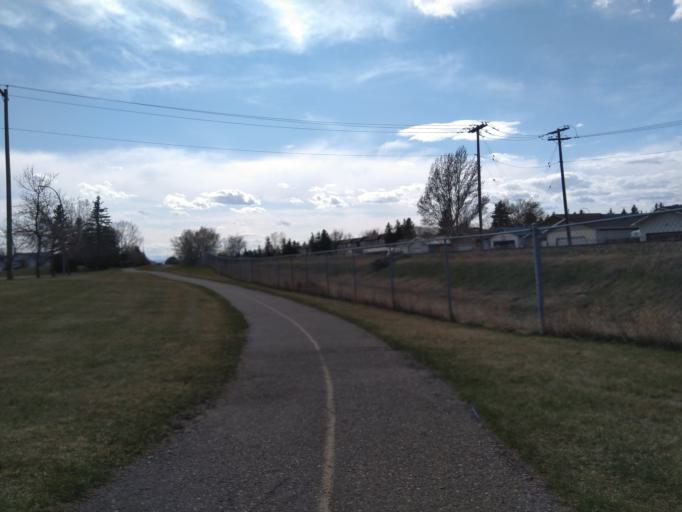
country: CA
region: Alberta
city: Chestermere
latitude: 51.0499
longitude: -113.9306
